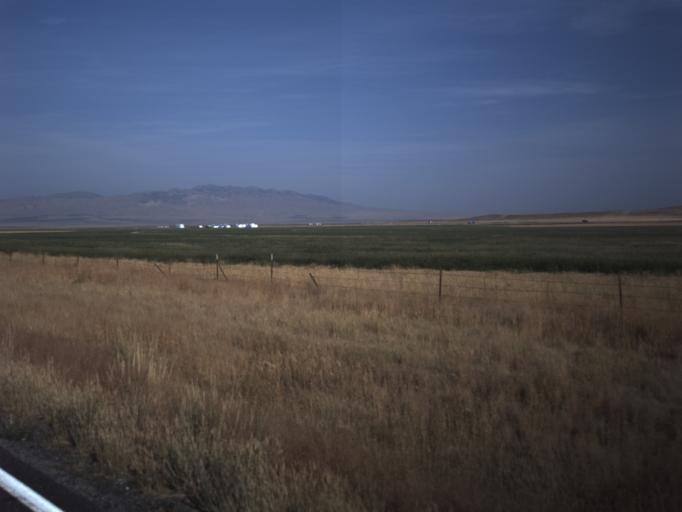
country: US
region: Idaho
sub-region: Oneida County
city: Malad City
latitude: 41.9668
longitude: -112.7876
